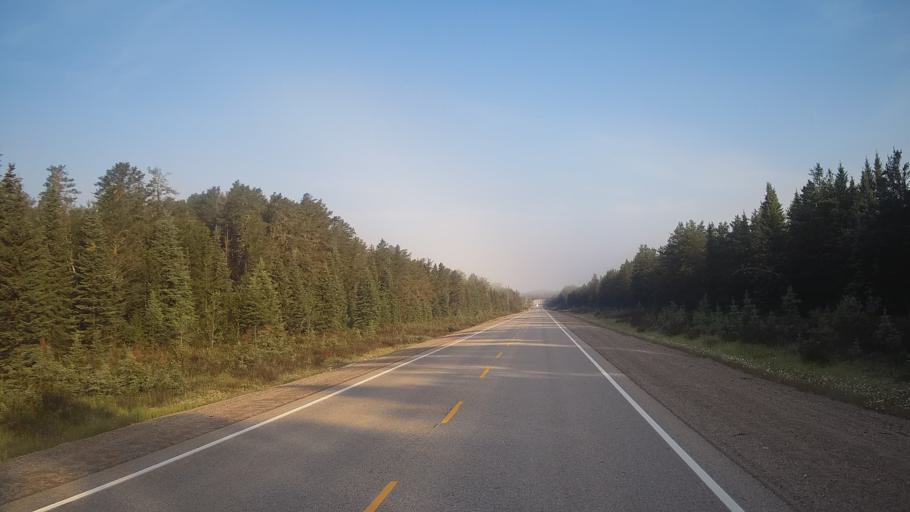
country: CA
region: Ontario
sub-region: Rainy River District
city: Atikokan
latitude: 49.3335
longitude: -91.4534
